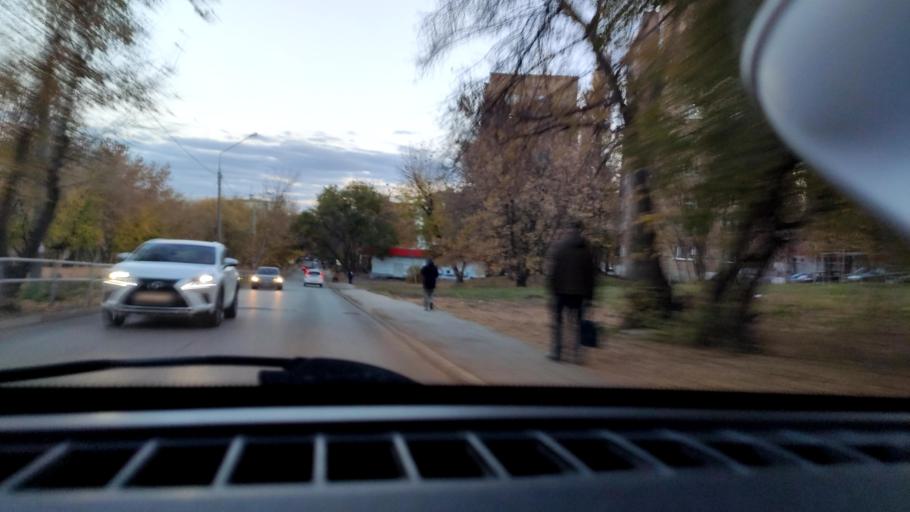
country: RU
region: Samara
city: Samara
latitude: 53.2422
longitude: 50.2214
